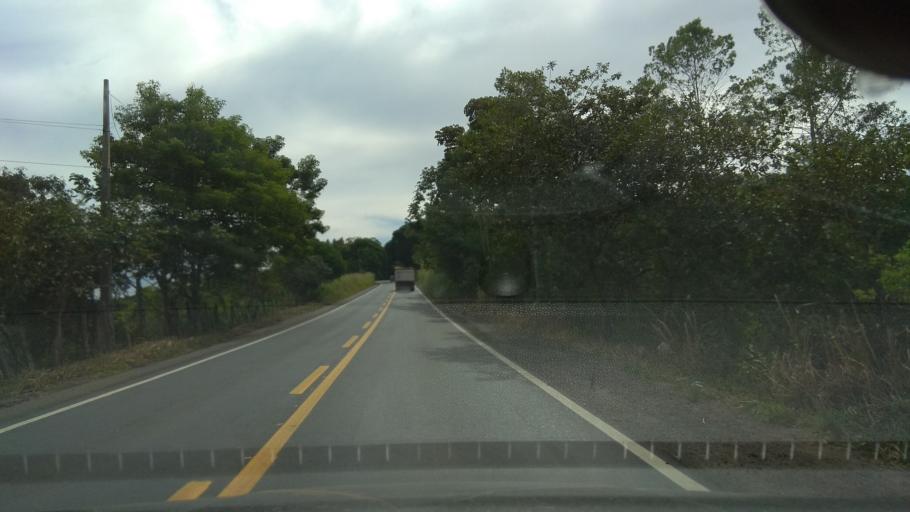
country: BR
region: Bahia
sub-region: Ubata
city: Ubata
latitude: -14.1993
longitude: -39.6100
